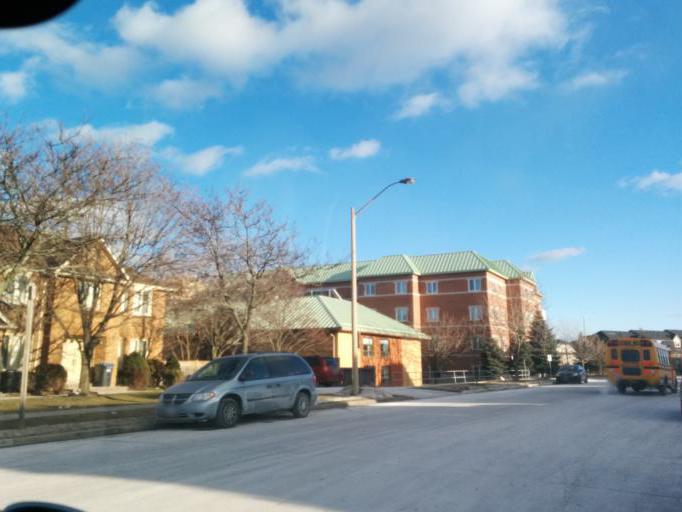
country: CA
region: Ontario
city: Mississauga
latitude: 43.6120
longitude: -79.6530
